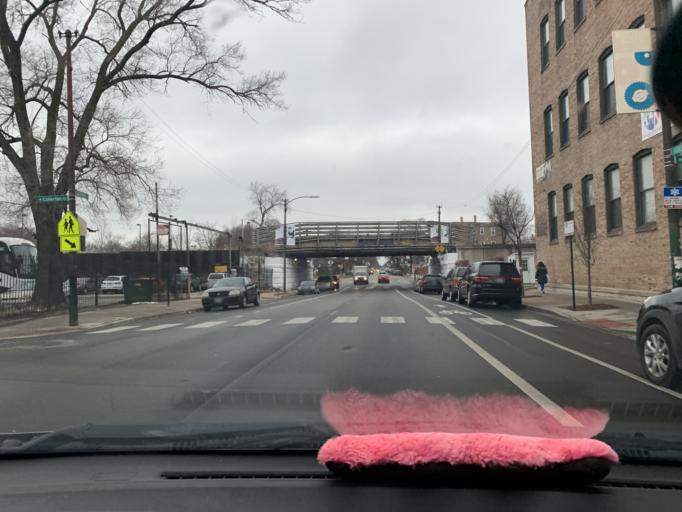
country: US
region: Illinois
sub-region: Cook County
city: Chicago
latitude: 41.8546
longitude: -87.6955
